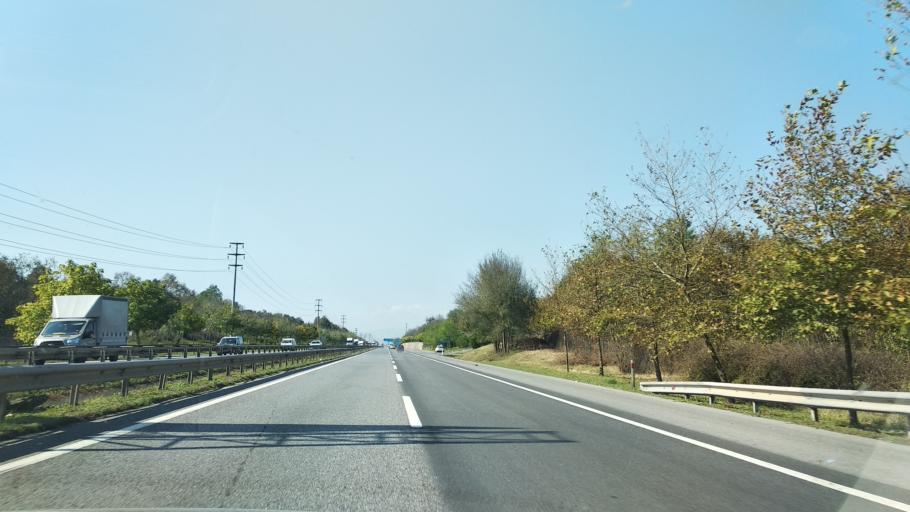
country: TR
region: Kocaeli
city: Derbent
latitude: 40.7406
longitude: 30.0933
